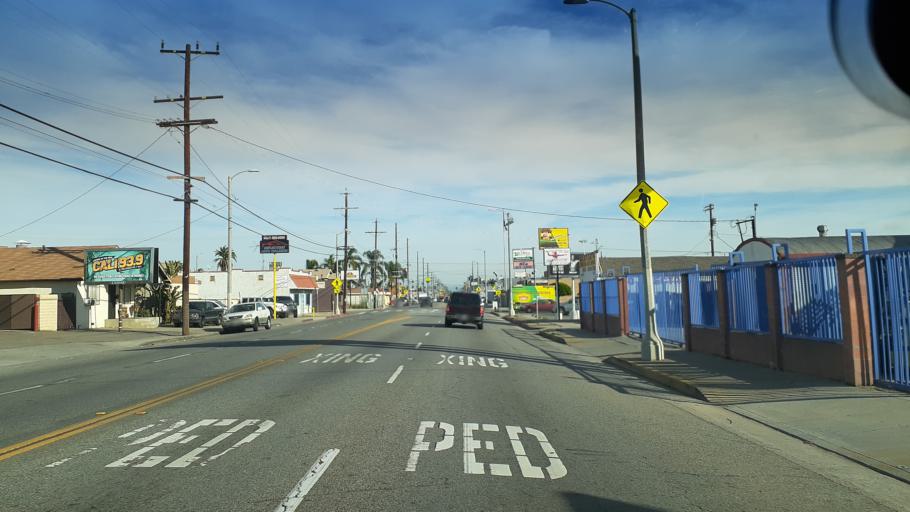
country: US
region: California
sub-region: Los Angeles County
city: Lomita
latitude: 33.7791
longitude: -118.2778
